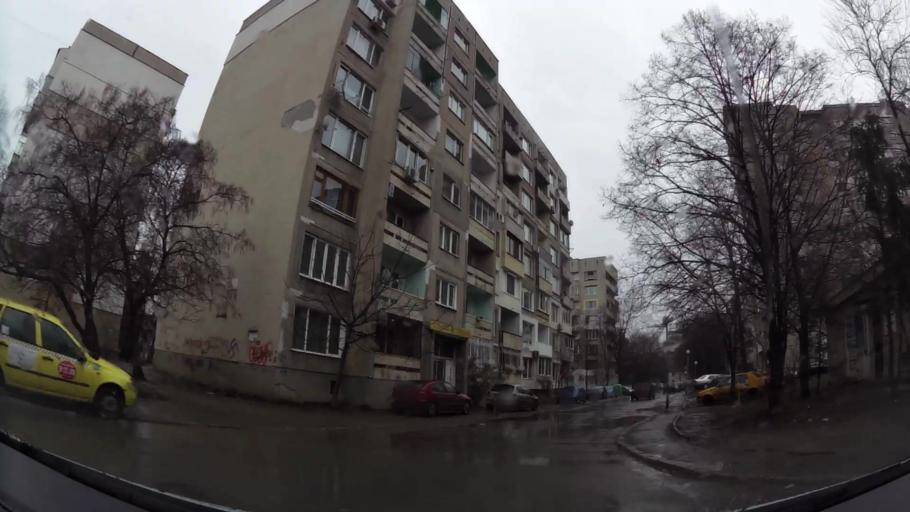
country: BG
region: Sofia-Capital
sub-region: Stolichna Obshtina
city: Sofia
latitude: 42.6618
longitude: 23.3613
